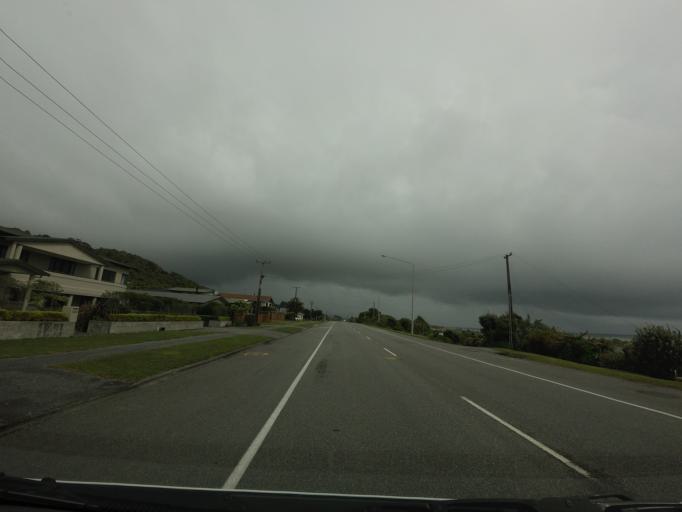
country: NZ
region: West Coast
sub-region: Grey District
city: Greymouth
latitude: -42.4813
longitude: 171.1837
